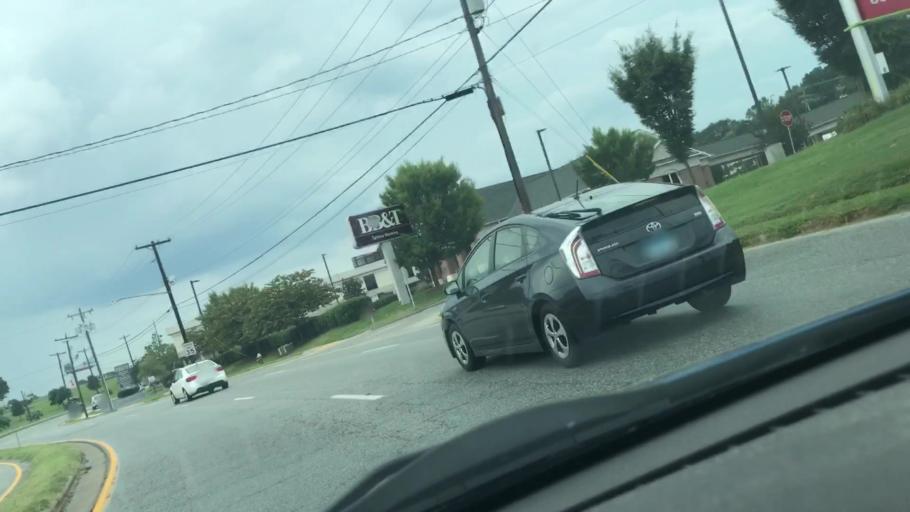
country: US
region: North Carolina
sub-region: Guilford County
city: Greensboro
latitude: 36.0859
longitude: -79.8061
